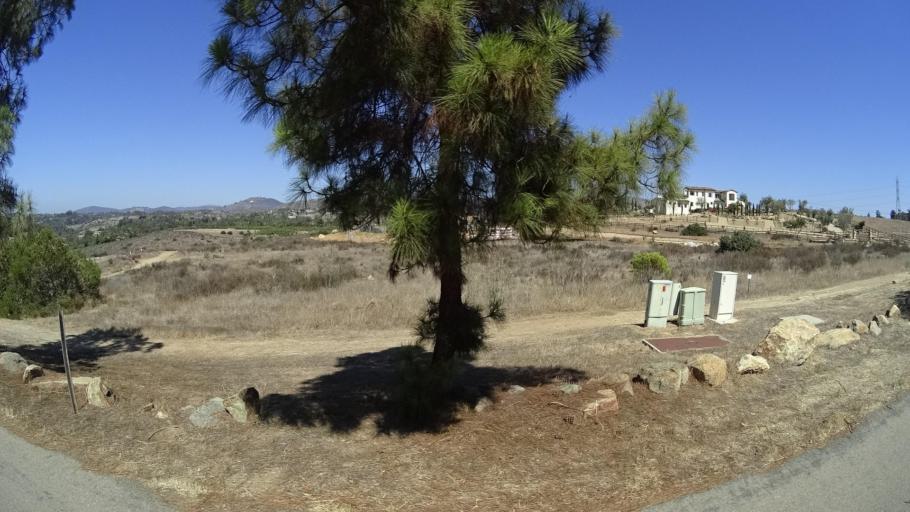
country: US
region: California
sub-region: San Diego County
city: Rancho Santa Fe
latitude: 33.0205
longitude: -117.1726
